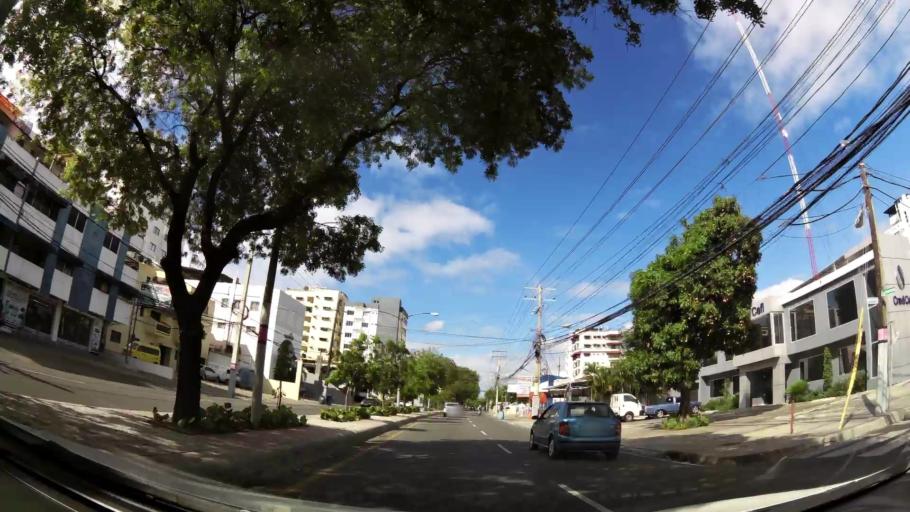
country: DO
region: Nacional
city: Bella Vista
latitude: 18.4536
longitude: -69.9471
